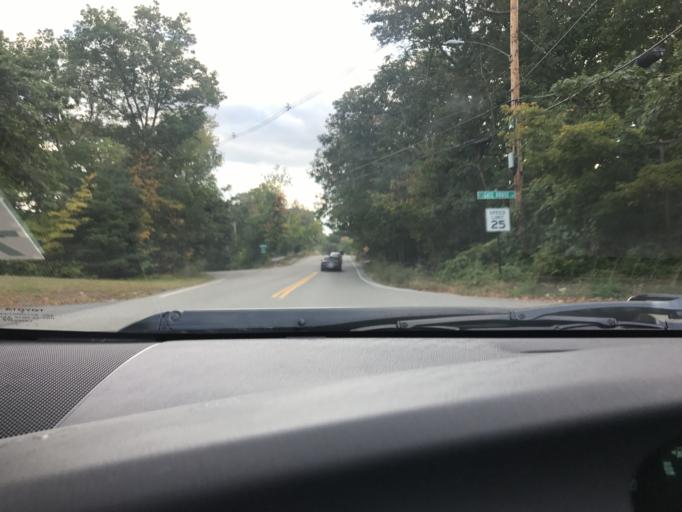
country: US
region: Massachusetts
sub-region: Middlesex County
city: Waltham
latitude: 42.3540
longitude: -71.2636
